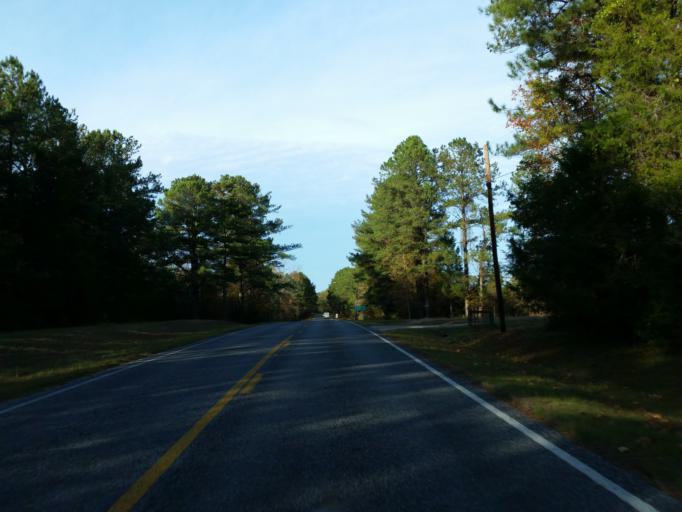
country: US
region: Mississippi
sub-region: Clarke County
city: Stonewall
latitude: 32.0468
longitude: -88.8828
